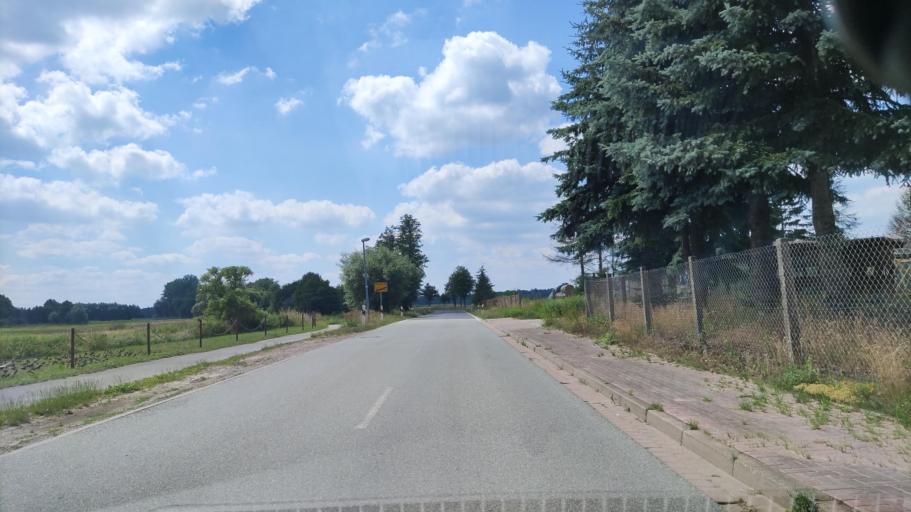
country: DE
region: Mecklenburg-Vorpommern
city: Lubtheen
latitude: 53.3367
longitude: 11.1382
